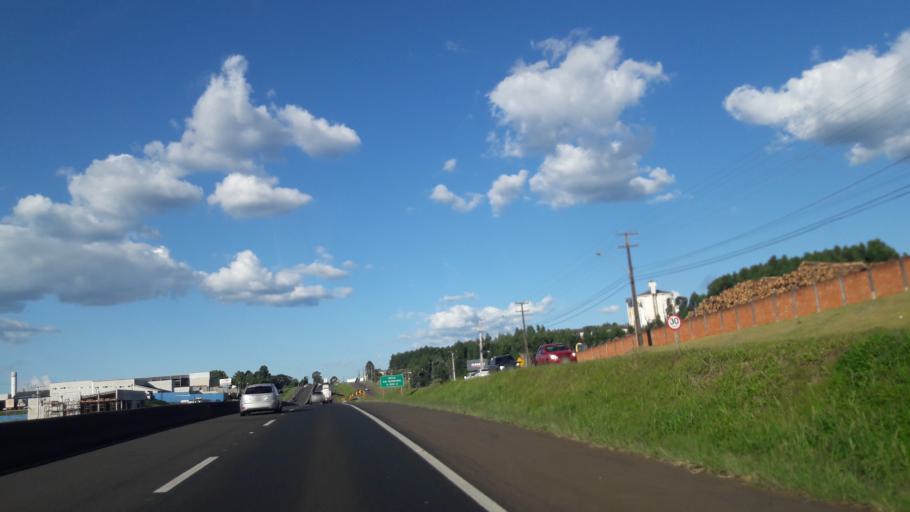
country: BR
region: Parana
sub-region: Guarapuava
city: Guarapuava
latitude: -25.3539
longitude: -51.4600
